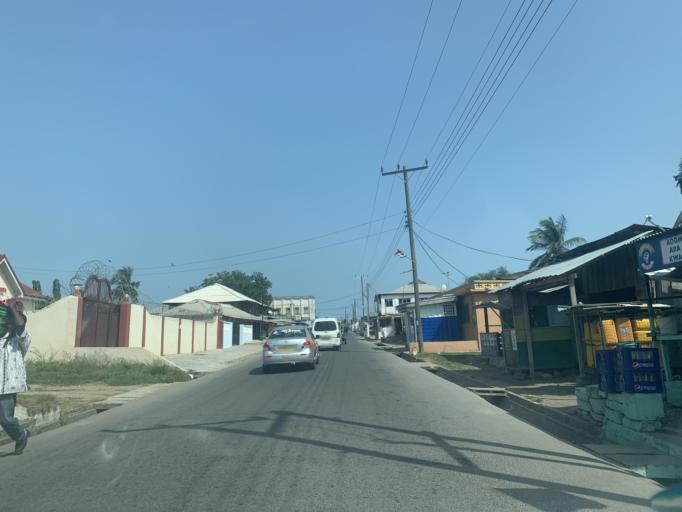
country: GH
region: Central
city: Winneba
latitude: 5.3454
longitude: -0.6283
